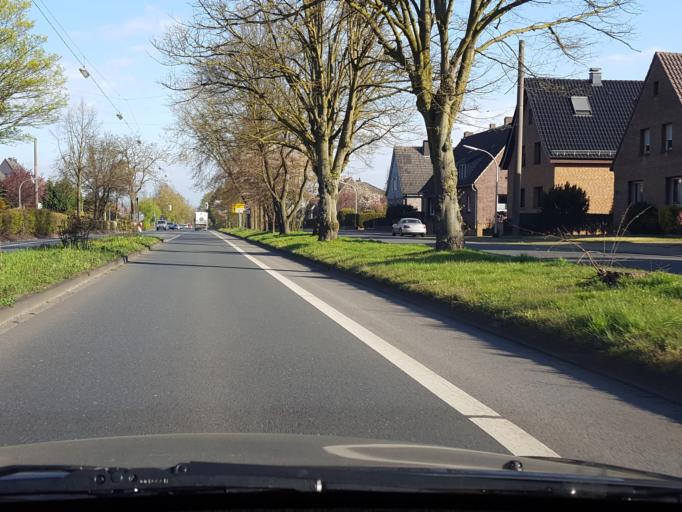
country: DE
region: North Rhine-Westphalia
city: Datteln
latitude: 51.6588
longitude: 7.3513
